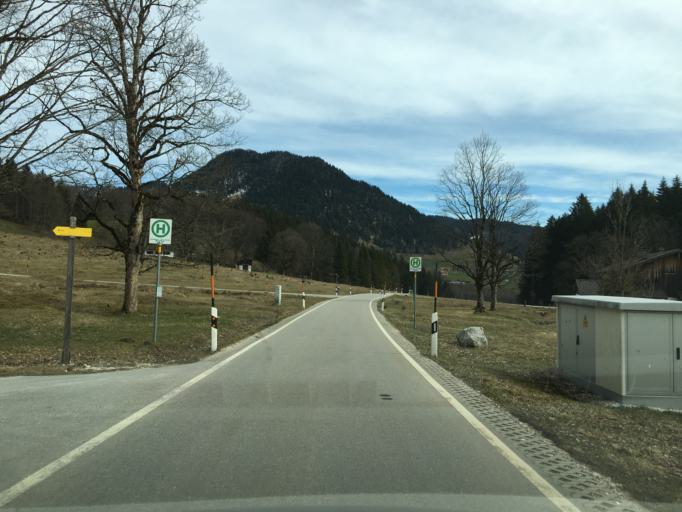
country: DE
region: Bavaria
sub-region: Upper Bavaria
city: Ramsau
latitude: 47.6134
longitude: 12.8630
